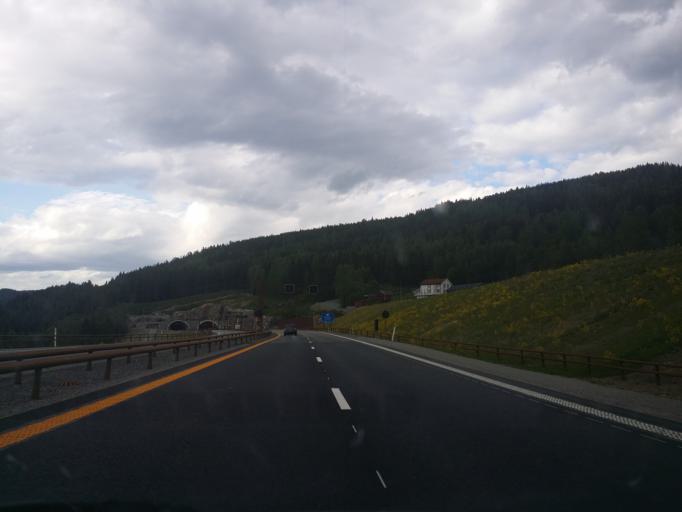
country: NO
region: Akershus
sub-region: Eidsvoll
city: Eidsvoll
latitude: 60.4597
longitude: 11.2417
